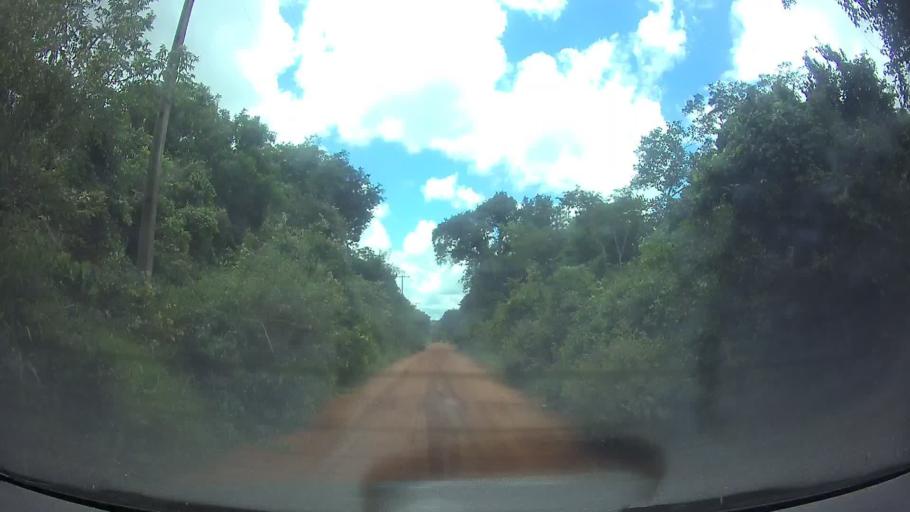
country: PY
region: Paraguari
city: La Colmena
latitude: -25.9453
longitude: -56.7801
